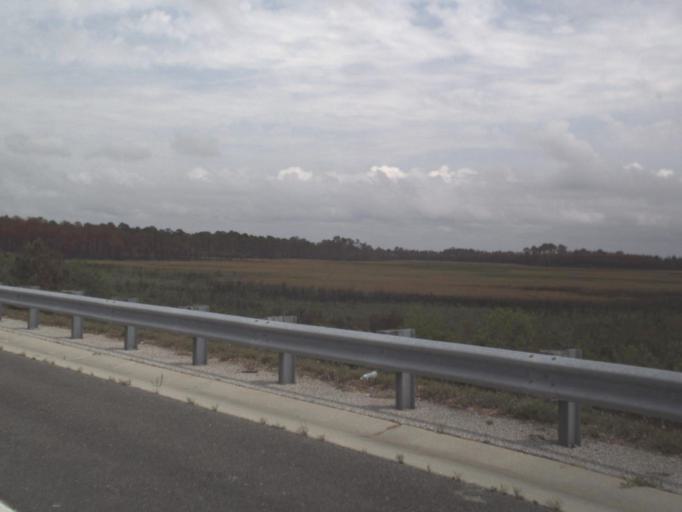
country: US
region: Florida
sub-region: Santa Rosa County
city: Oriole Beach
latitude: 30.4445
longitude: -87.1005
